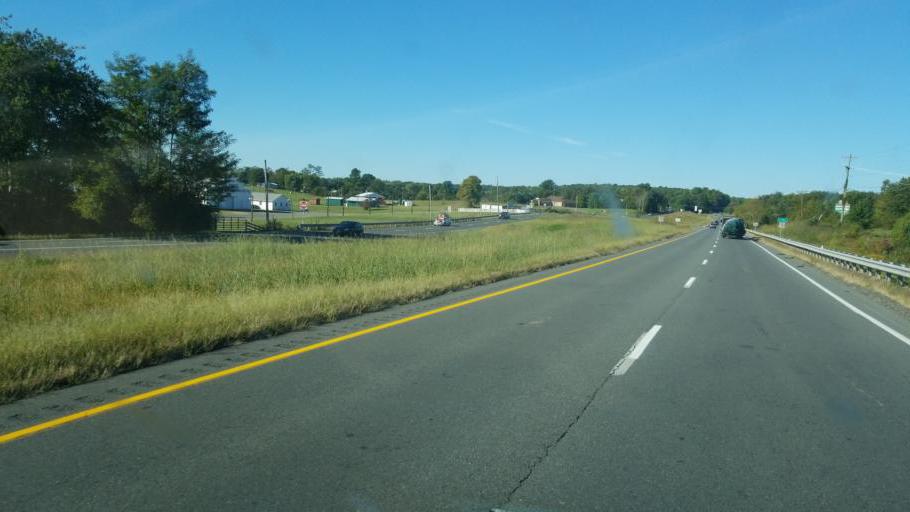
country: US
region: Virginia
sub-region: Culpeper County
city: Merrimac
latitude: 38.4572
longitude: -78.0548
